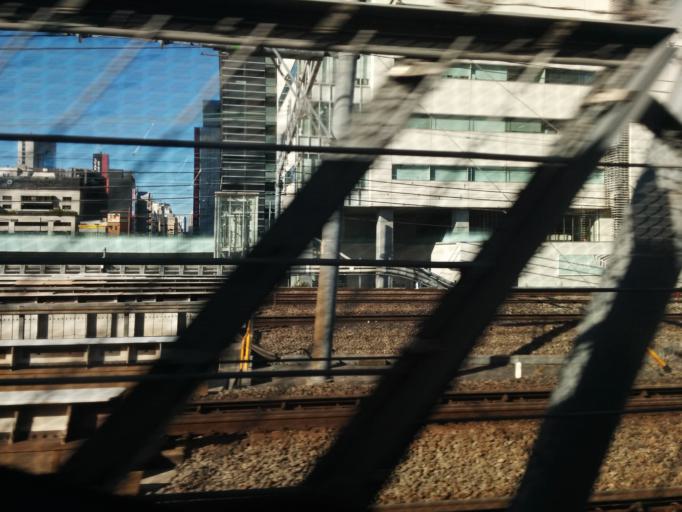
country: JP
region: Tokyo
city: Tokyo
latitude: 35.6565
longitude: 139.7575
